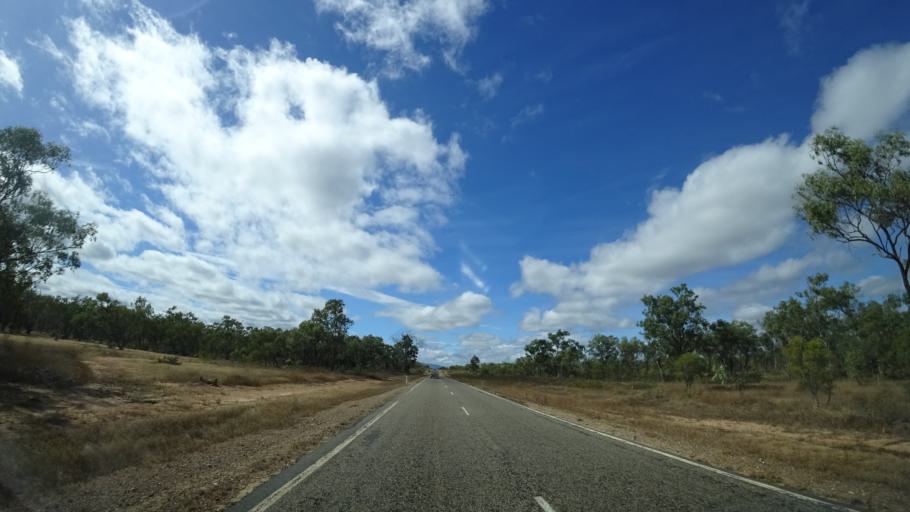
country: AU
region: Queensland
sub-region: Cairns
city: Port Douglas
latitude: -16.4954
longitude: 144.9652
